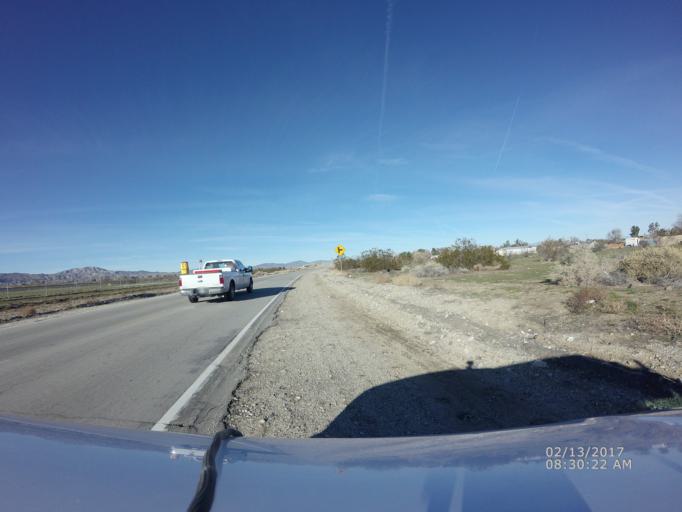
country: US
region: California
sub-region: Los Angeles County
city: Littlerock
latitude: 34.5430
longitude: -117.9469
